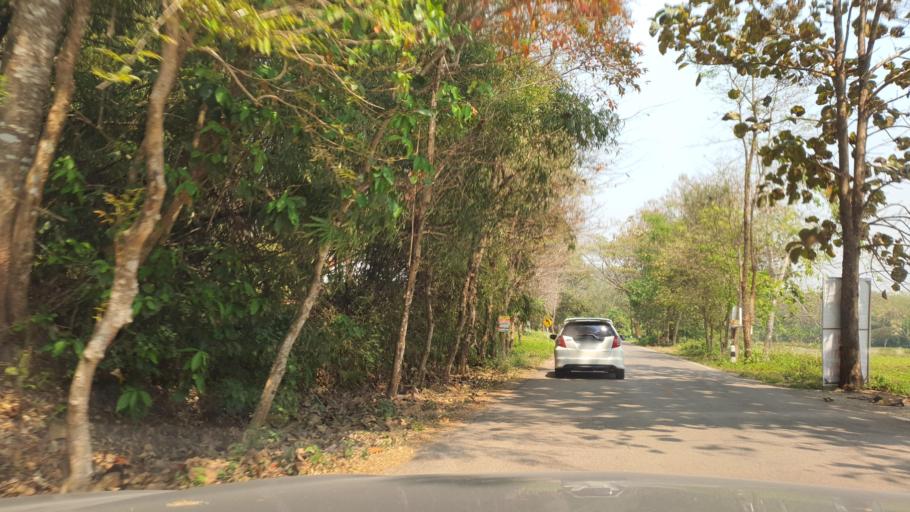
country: TH
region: Chiang Rai
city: Mae Lao
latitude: 19.7483
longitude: 99.6324
